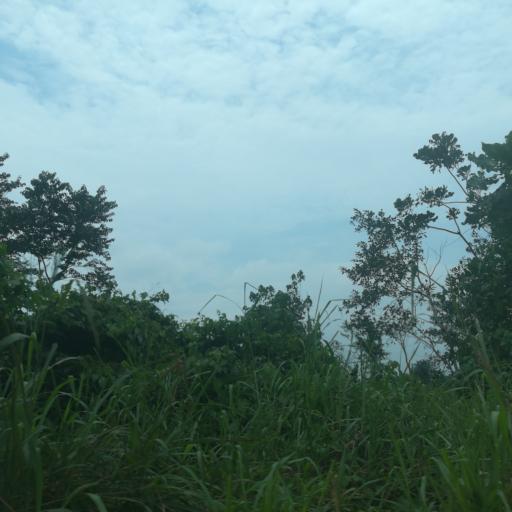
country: NG
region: Lagos
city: Ejirin
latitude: 6.6484
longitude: 3.7397
